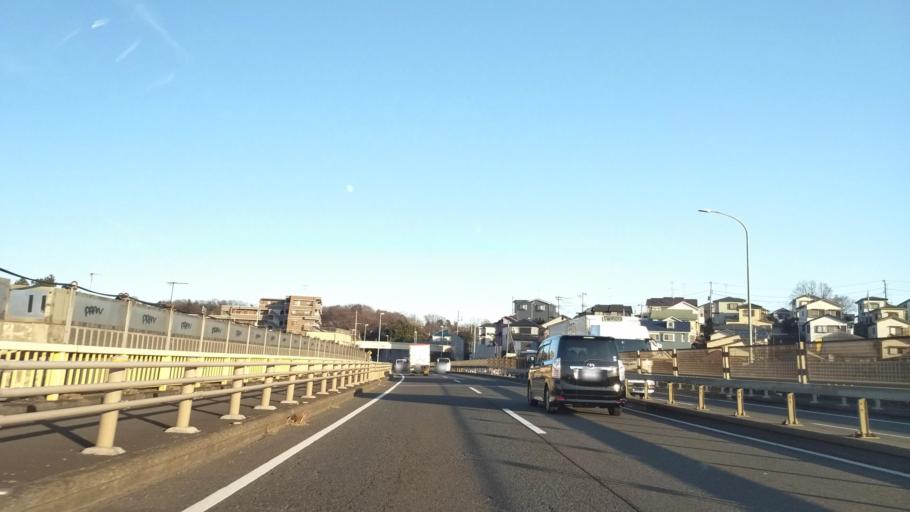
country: JP
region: Kanagawa
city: Zama
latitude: 35.4638
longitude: 139.3998
